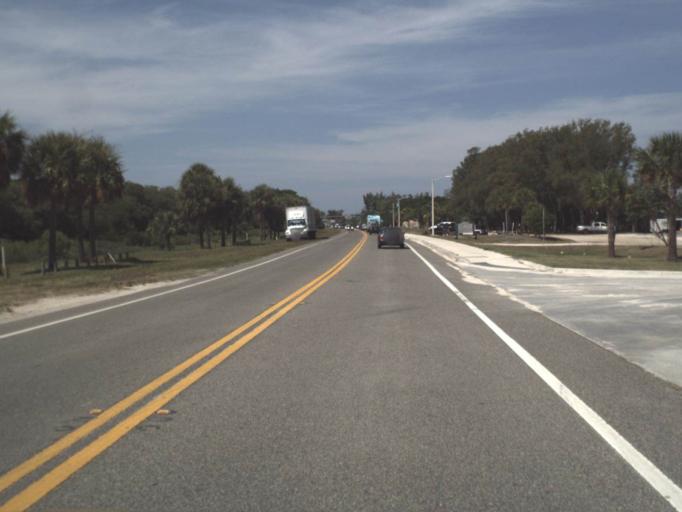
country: US
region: Florida
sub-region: Manatee County
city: Holmes Beach
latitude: 27.4971
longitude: -82.7015
